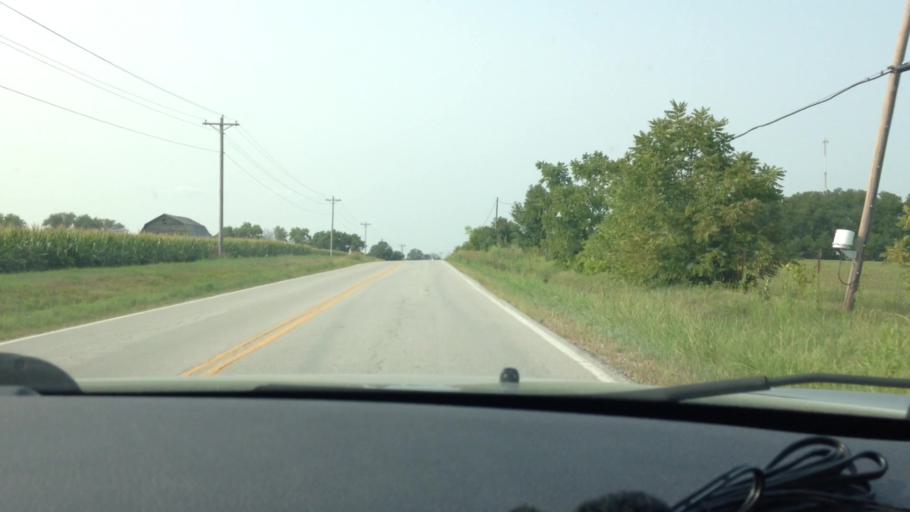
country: US
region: Missouri
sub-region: Platte County
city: Platte City
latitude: 39.4089
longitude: -94.7963
